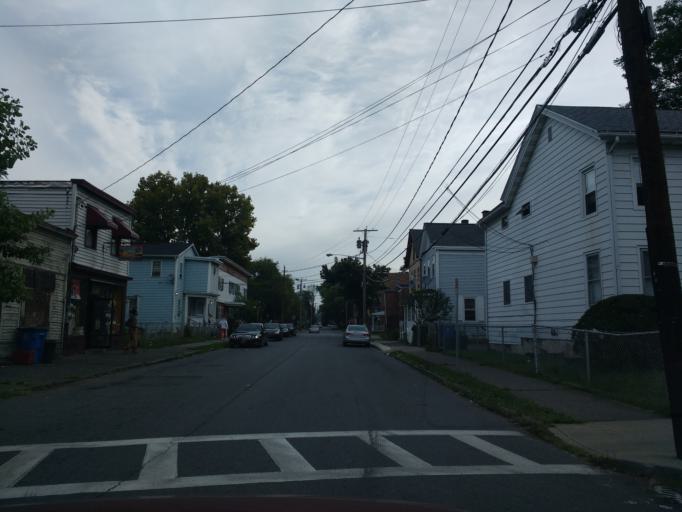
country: US
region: New York
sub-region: Ulster County
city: Kingston
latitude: 41.9289
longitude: -74.0118
